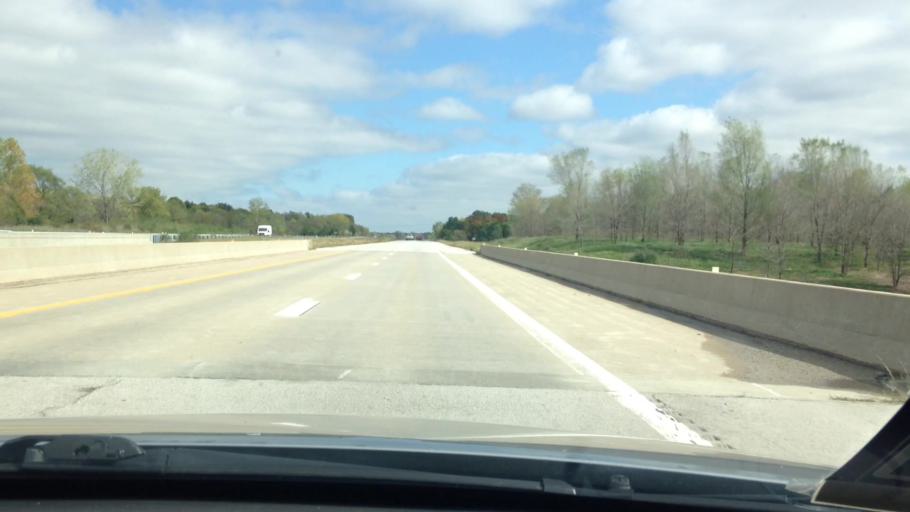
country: US
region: Missouri
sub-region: Platte County
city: Weatherby Lake
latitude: 39.2475
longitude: -94.7341
